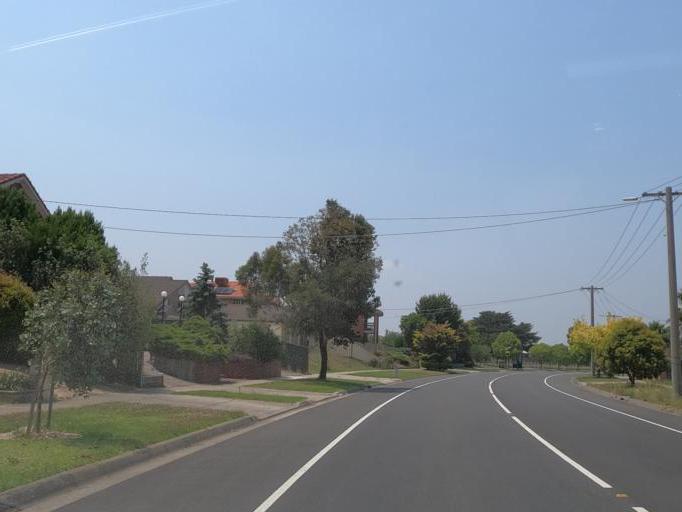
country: AU
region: Victoria
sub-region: Hume
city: Meadow Heights
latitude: -37.6418
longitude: 144.8943
